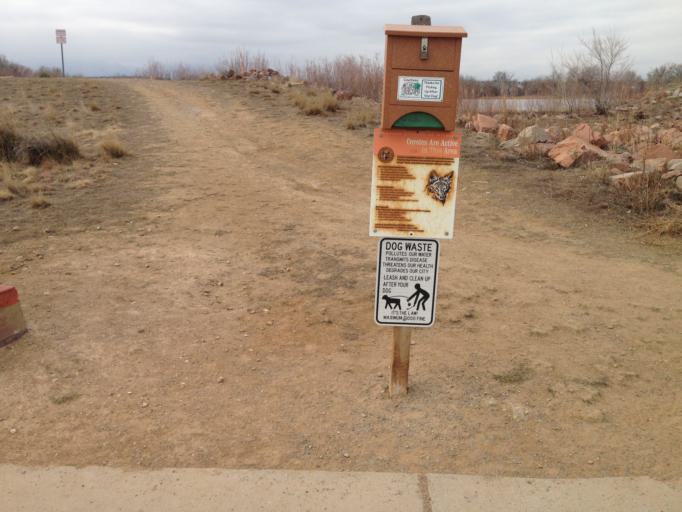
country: US
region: Colorado
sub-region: Boulder County
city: Lafayette
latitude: 39.9945
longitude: -105.1089
